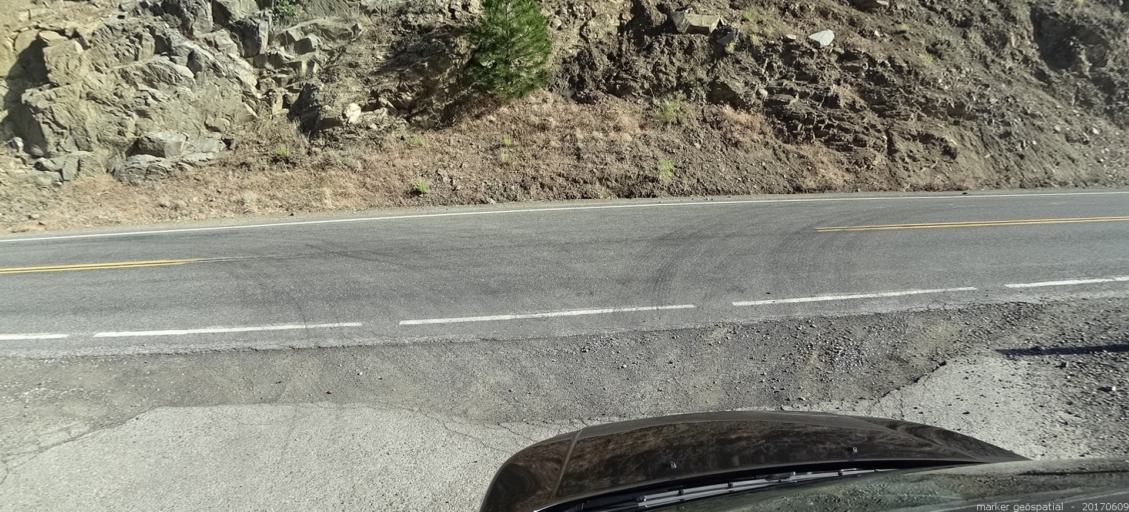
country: US
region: California
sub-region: Siskiyou County
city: Weed
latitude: 41.3112
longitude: -122.7642
